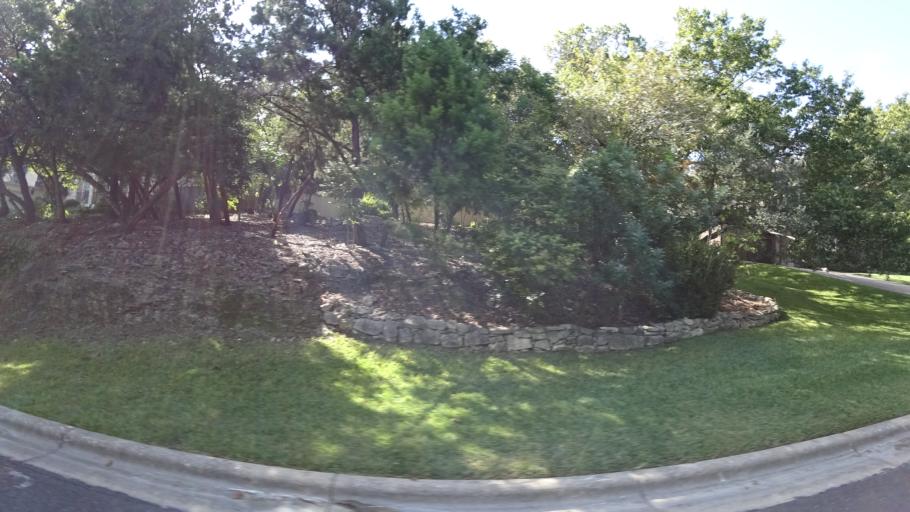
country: US
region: Texas
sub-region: Travis County
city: West Lake Hills
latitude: 30.3506
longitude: -97.7686
